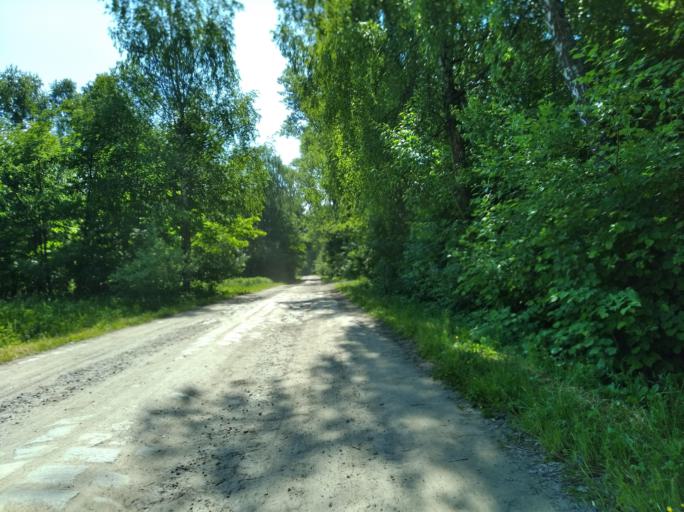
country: PL
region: Subcarpathian Voivodeship
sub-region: Powiat krosnienski
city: Odrzykon
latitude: 49.7708
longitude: 21.7668
